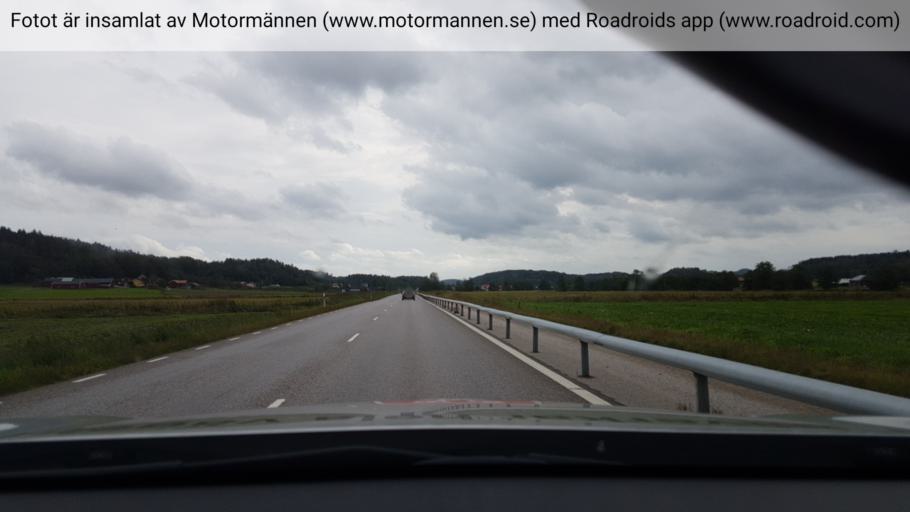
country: SE
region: Vaestra Goetaland
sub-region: Munkedals Kommun
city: Munkedal
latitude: 58.5164
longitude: 11.5757
